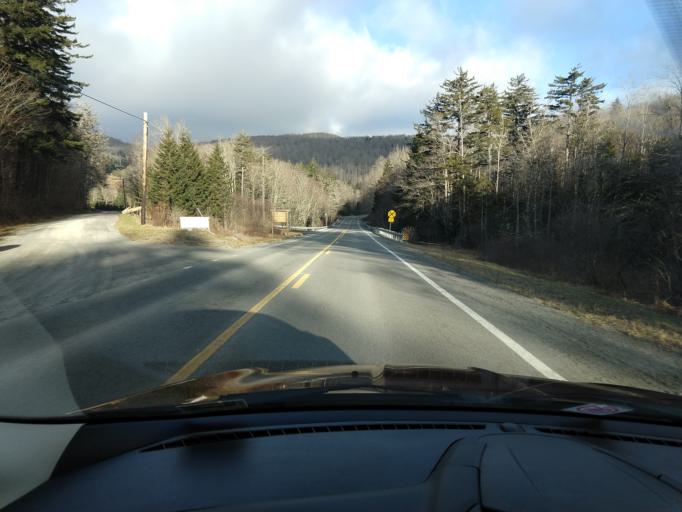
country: US
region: West Virginia
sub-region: Randolph County
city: Elkins
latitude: 38.6165
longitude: -79.8695
